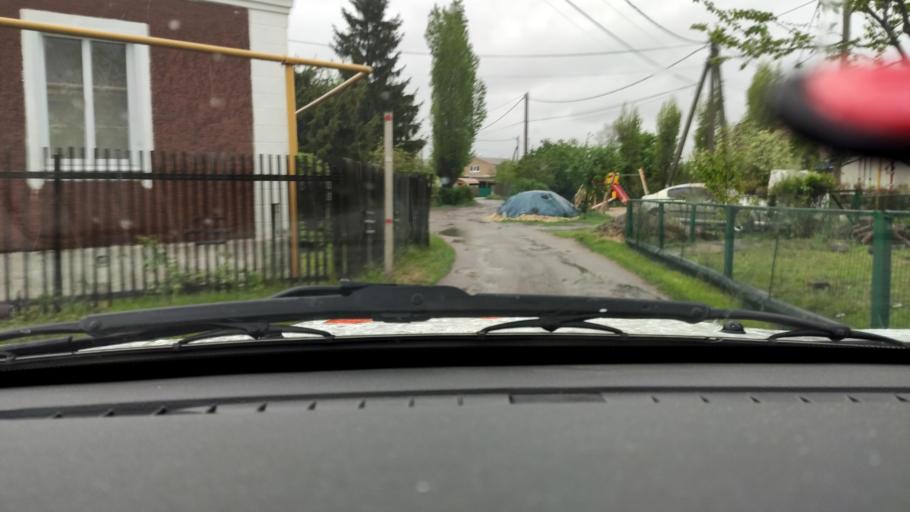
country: RU
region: Voronezj
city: Novaya Usman'
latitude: 51.6323
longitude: 39.3939
